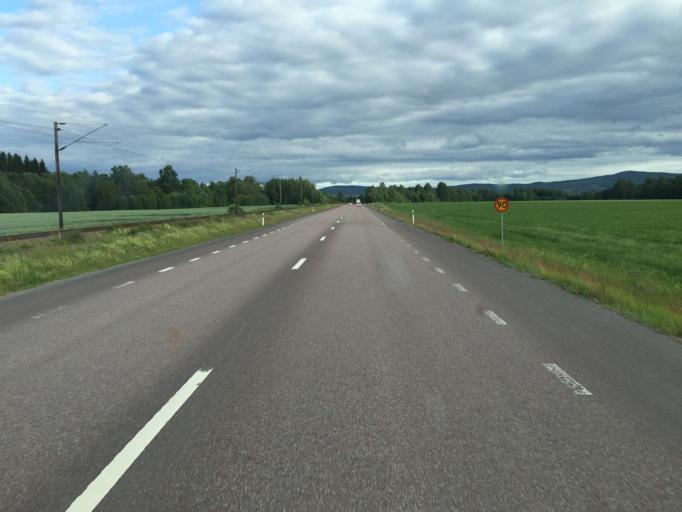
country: SE
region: Dalarna
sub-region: Gagnefs Kommun
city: Djuras
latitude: 60.5741
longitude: 15.1236
